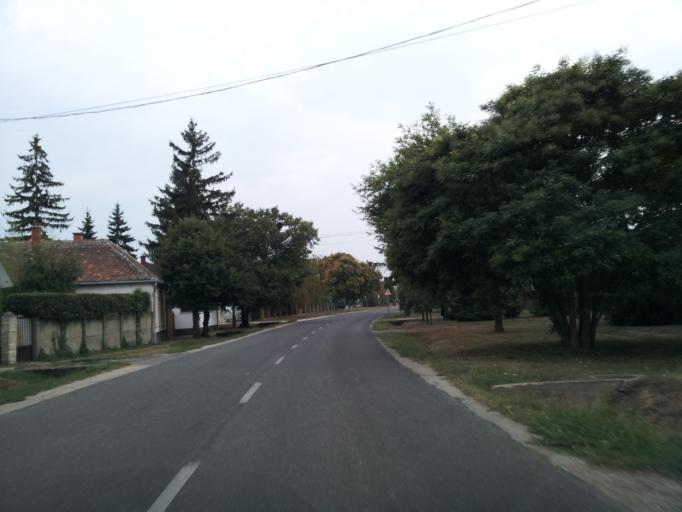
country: HU
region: Vas
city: Sarvar
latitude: 47.2067
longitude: 16.8946
